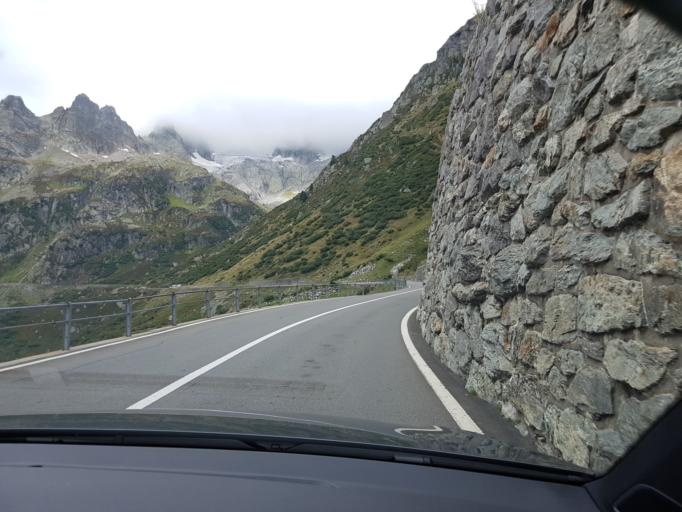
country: CH
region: Obwalden
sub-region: Obwalden
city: Engelberg
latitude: 46.7471
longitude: 8.4768
